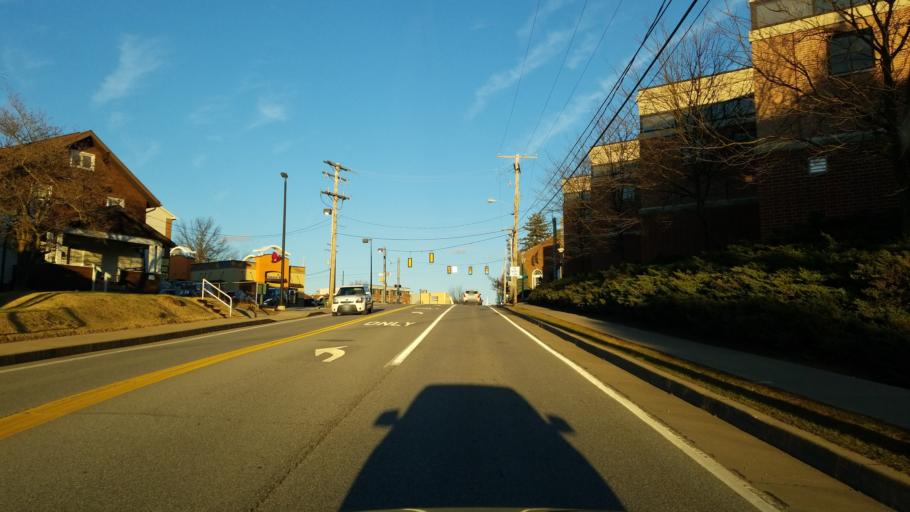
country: US
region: Pennsylvania
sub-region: Indiana County
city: Indiana
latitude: 40.6179
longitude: -79.1618
